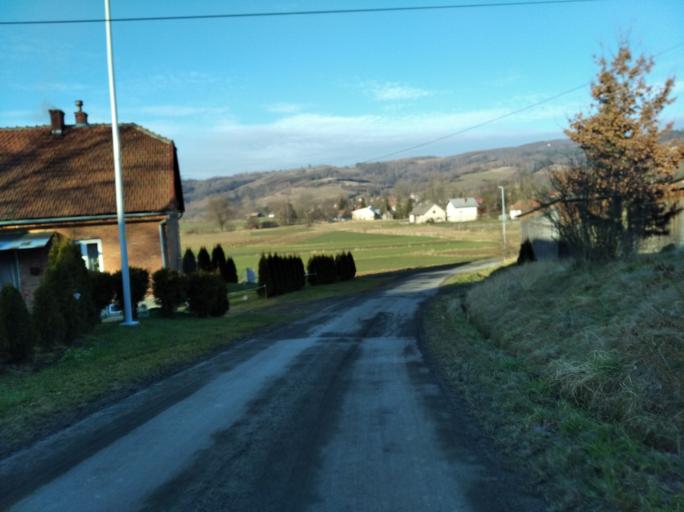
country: PL
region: Subcarpathian Voivodeship
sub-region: Powiat strzyzowski
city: Strzyzow
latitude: 49.8312
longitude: 21.8344
